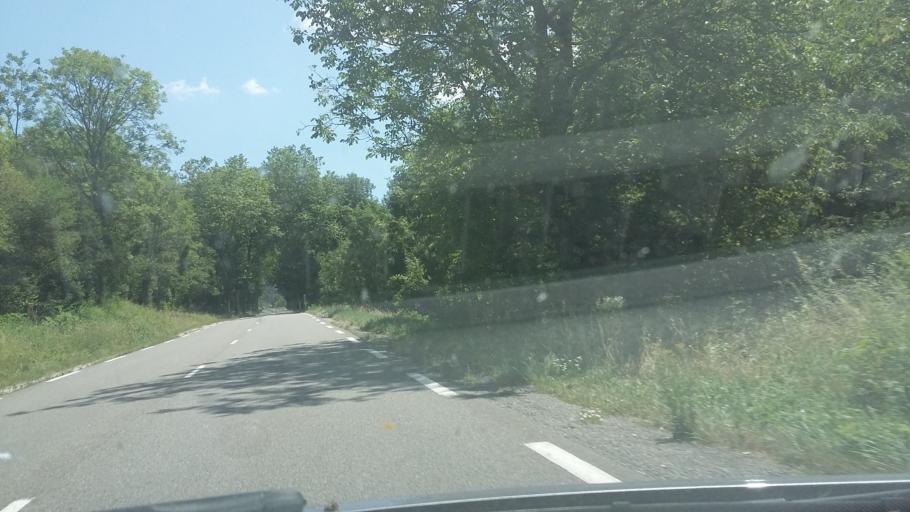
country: FR
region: Rhone-Alpes
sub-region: Departement de l'Ain
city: Virieu-le-Grand
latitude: 45.8393
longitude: 5.5817
